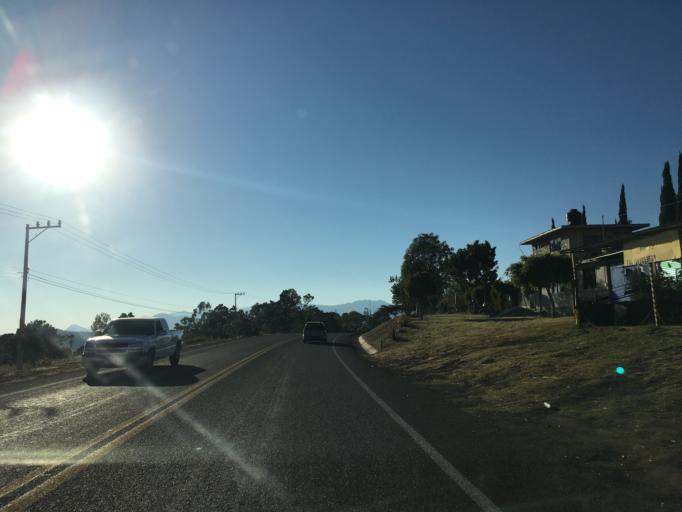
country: MX
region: Michoacan
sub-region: Zitacuaro
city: Puentecillas (Tercera Manzana de Zirahuato)
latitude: 19.4794
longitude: -100.4298
